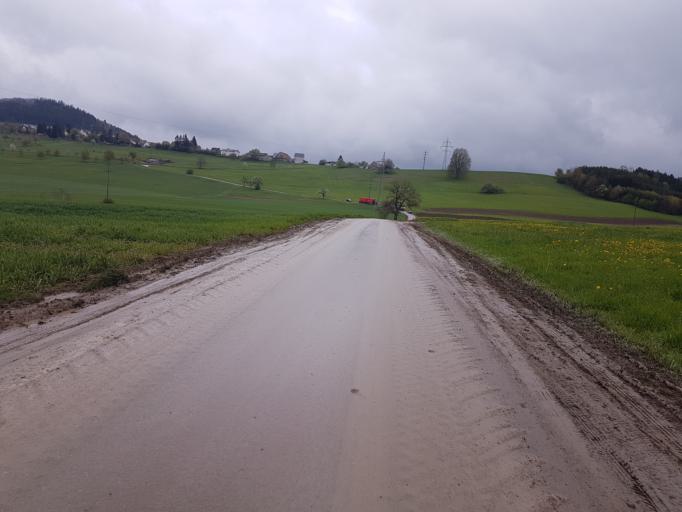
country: DE
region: Baden-Wuerttemberg
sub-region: Freiburg Region
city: Blumberg
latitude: 47.8971
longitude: 8.5422
